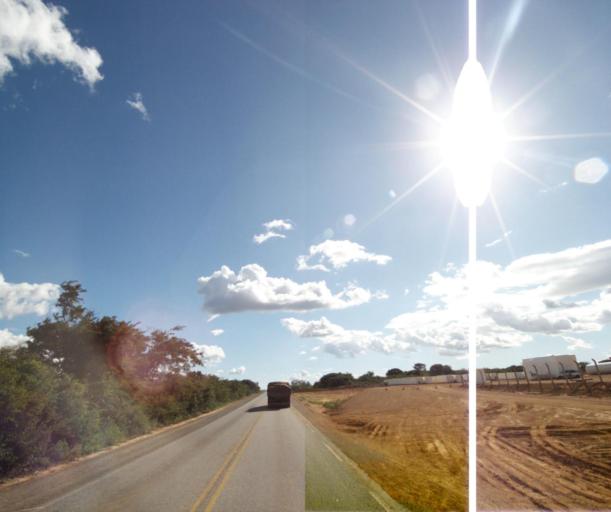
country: BR
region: Bahia
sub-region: Guanambi
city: Guanambi
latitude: -14.1377
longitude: -42.6388
